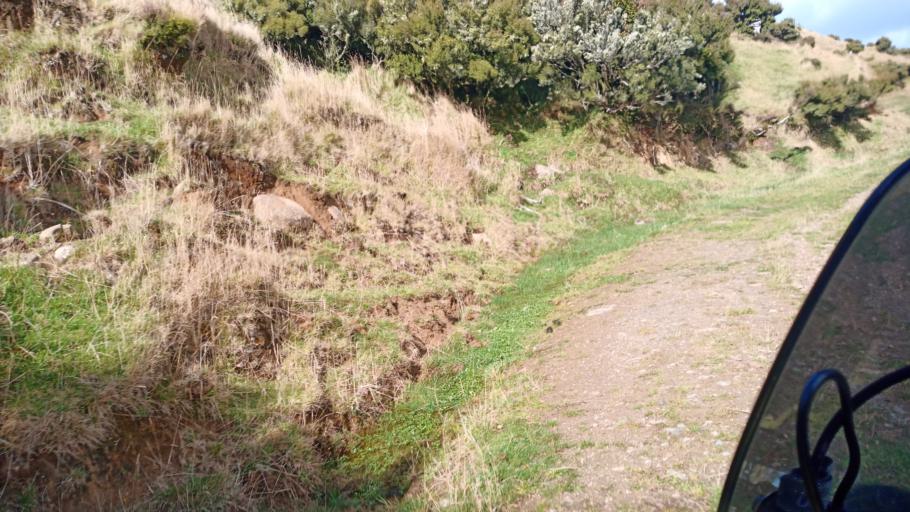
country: NZ
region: Gisborne
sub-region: Gisborne District
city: Gisborne
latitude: -38.4729
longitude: 177.5355
